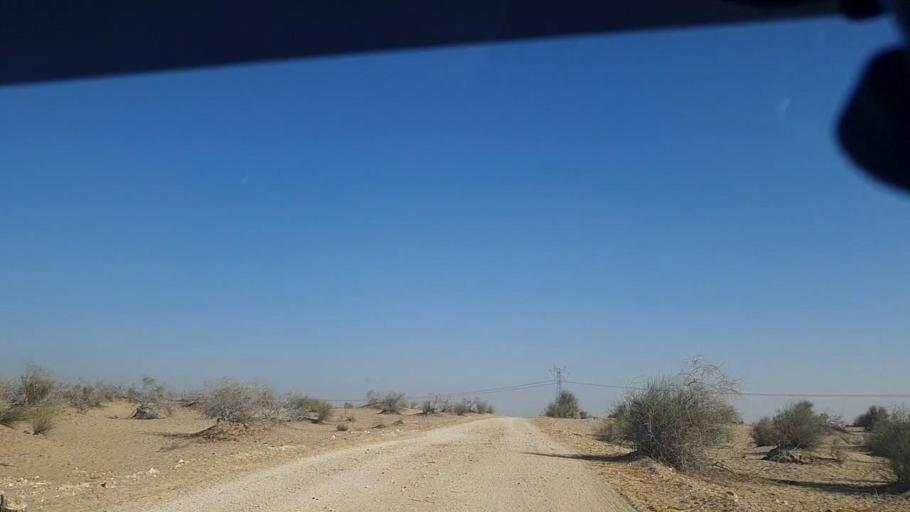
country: PK
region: Sindh
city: Khanpur
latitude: 27.6461
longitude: 69.3992
